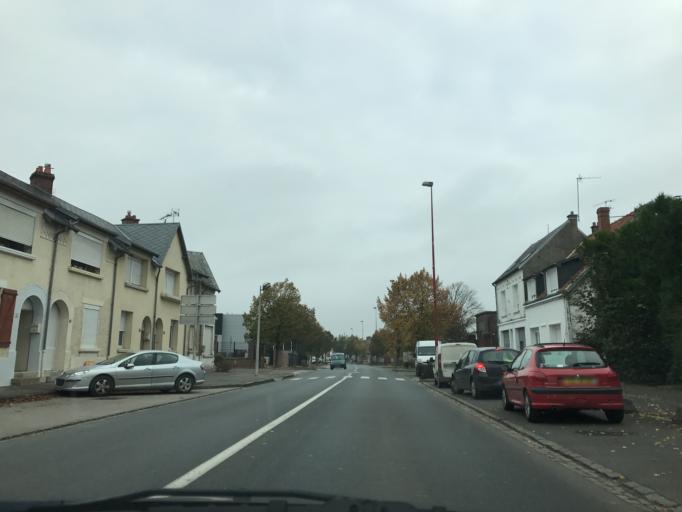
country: FR
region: Picardie
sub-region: Departement de la Somme
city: Peronne
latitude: 49.9136
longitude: 2.9337
